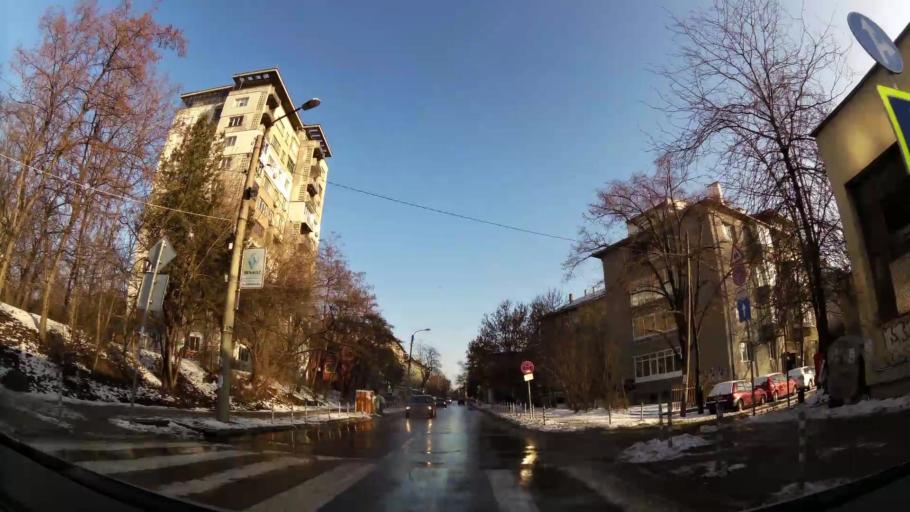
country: BG
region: Sofia-Capital
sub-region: Stolichna Obshtina
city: Sofia
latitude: 42.6866
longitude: 23.3531
